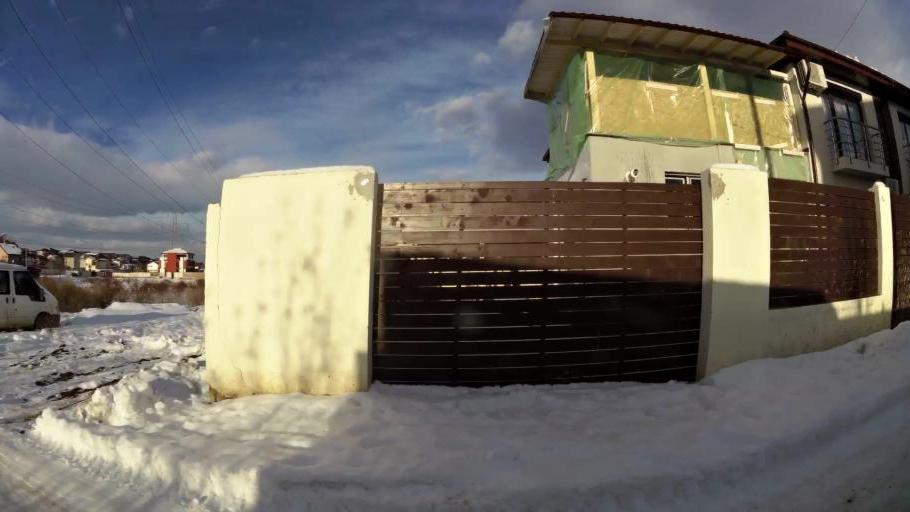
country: RO
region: Ilfov
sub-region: Comuna Fundeni-Dobroesti
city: Fundeni
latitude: 44.4632
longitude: 26.1738
